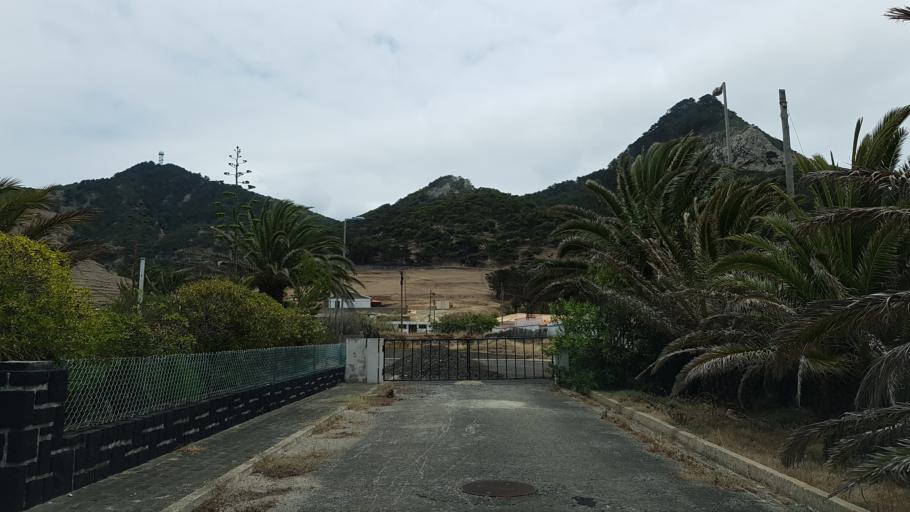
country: PT
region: Madeira
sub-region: Porto Santo
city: Camacha
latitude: 33.0868
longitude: -16.3392
